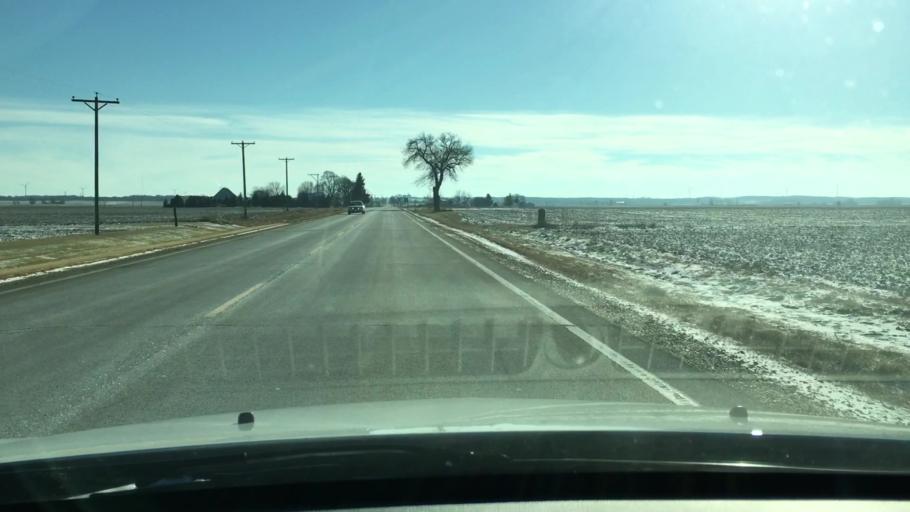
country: US
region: Illinois
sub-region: Ogle County
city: Rochelle
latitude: 41.7672
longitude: -89.0837
